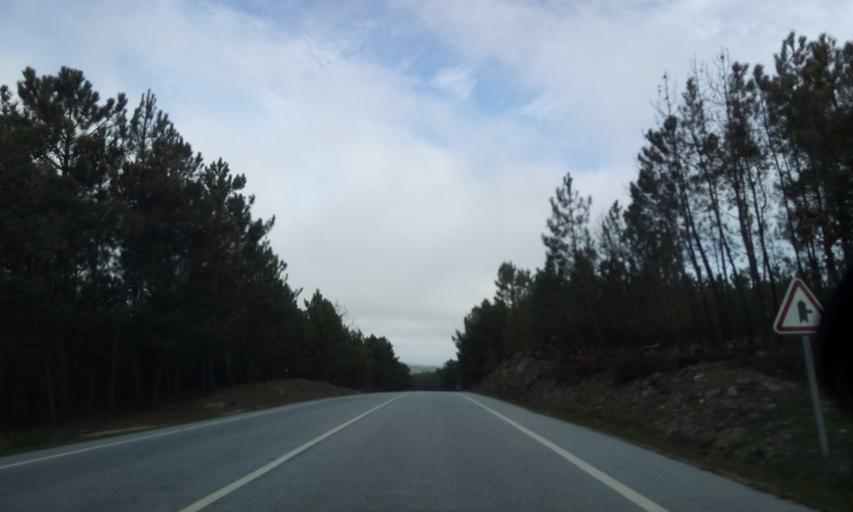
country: PT
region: Guarda
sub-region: Aguiar da Beira
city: Aguiar da Beira
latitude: 40.7978
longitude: -7.5202
